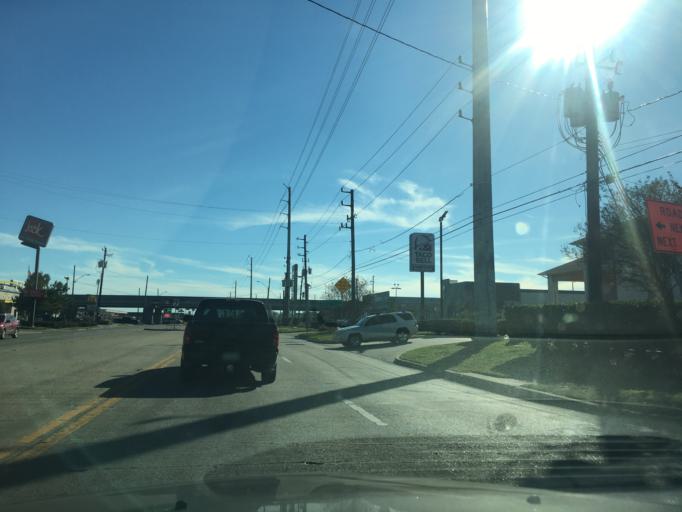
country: US
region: Texas
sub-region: Fort Bend County
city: Rosenberg
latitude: 29.5340
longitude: -95.8084
